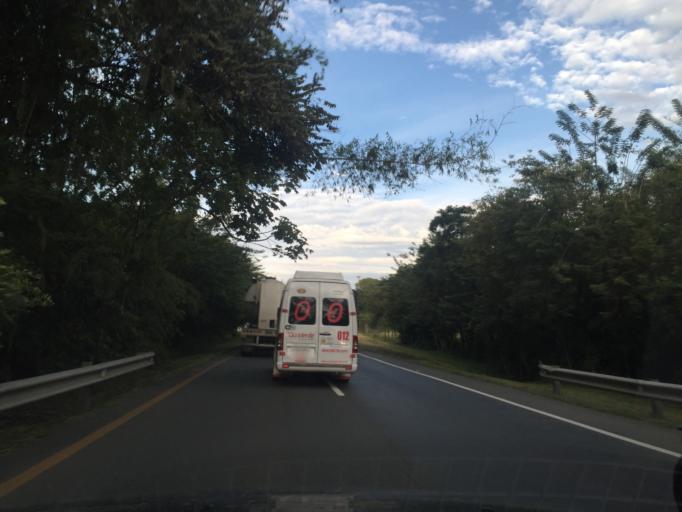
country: CO
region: Valle del Cauca
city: Bugalagrande
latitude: 4.2457
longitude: -76.1228
